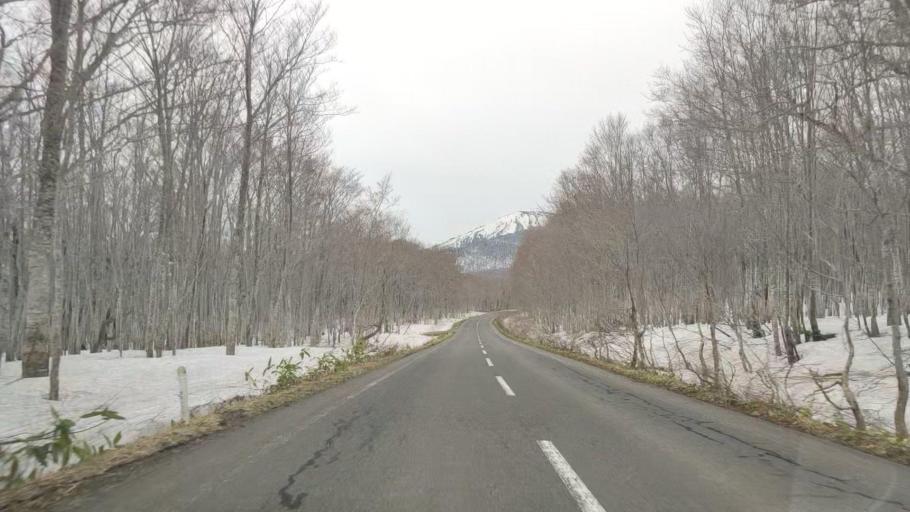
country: JP
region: Aomori
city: Aomori Shi
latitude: 40.6370
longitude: 140.9306
